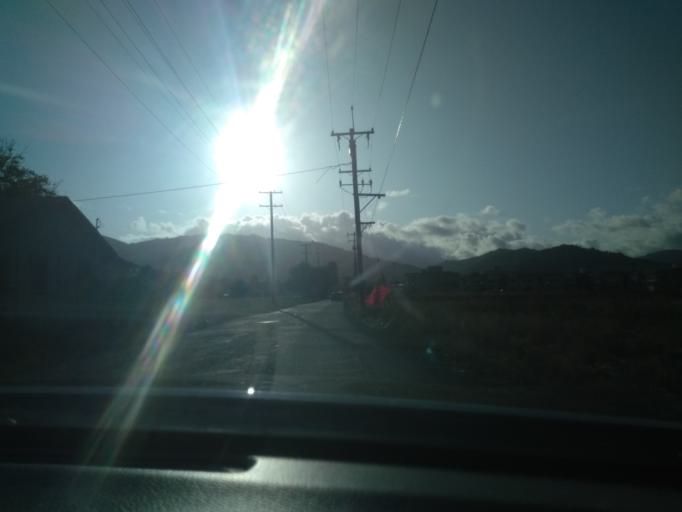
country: US
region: California
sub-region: Mendocino County
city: Ukiah
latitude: 39.1594
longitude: -123.2000
